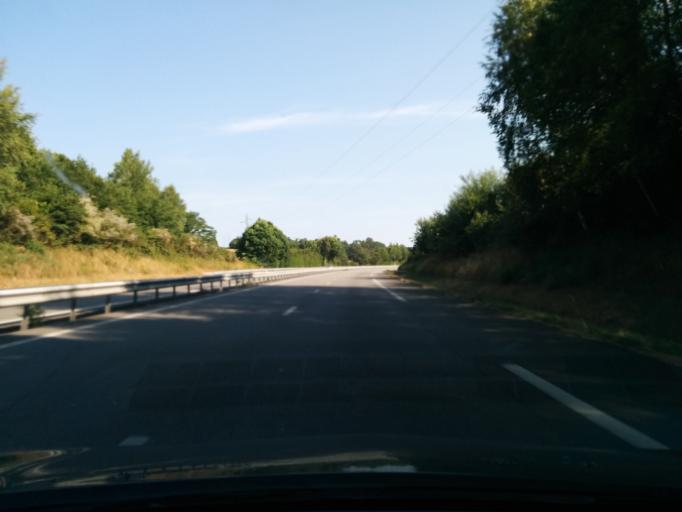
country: FR
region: Limousin
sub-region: Departement de la Haute-Vienne
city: Saint-Germain-les-Belles
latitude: 45.6208
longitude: 1.4466
